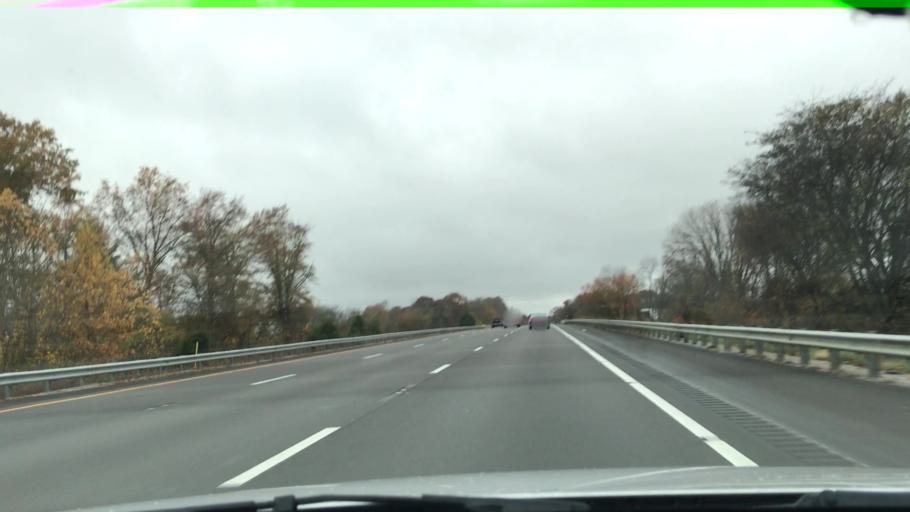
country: US
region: Kentucky
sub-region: Edmonson County
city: Brownsville
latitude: 37.0197
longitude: -86.2583
